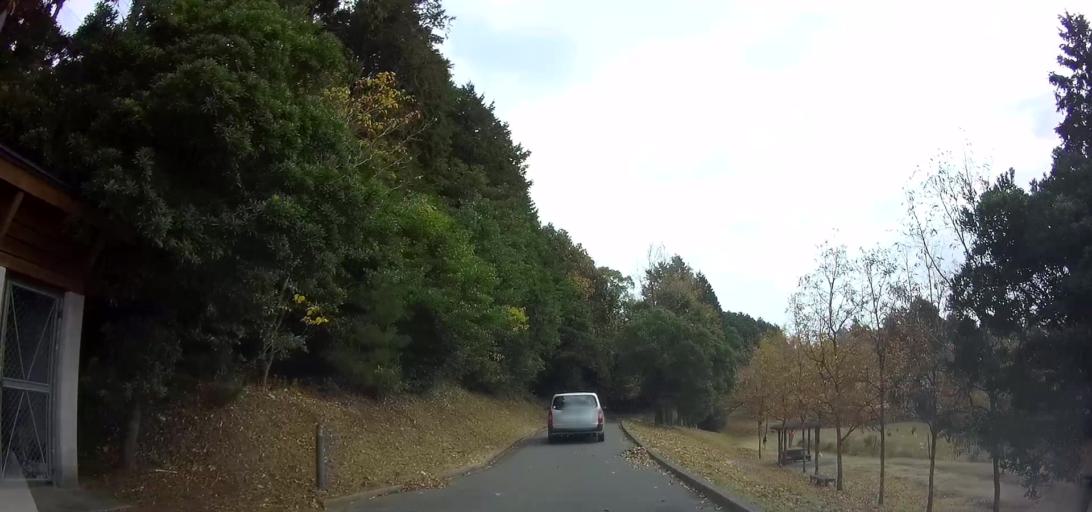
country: JP
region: Nagasaki
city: Shimabara
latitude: 32.7042
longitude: 130.2415
